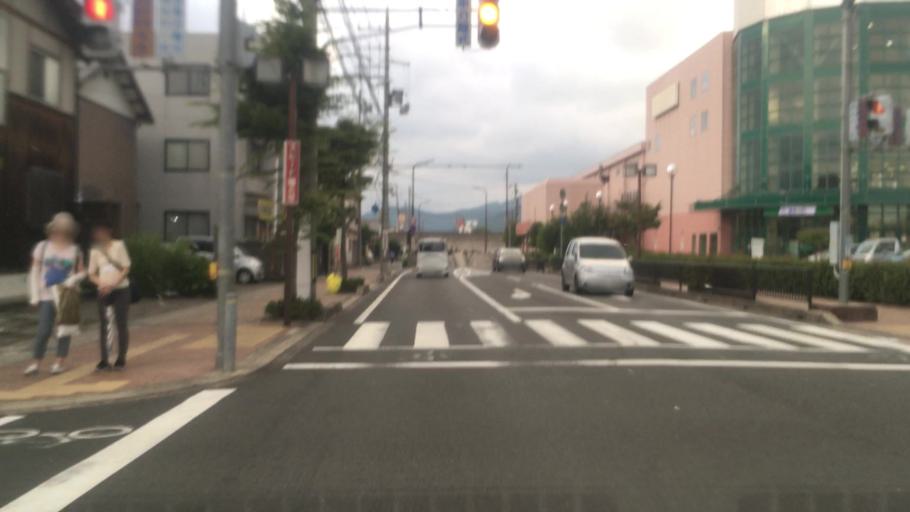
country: JP
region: Hyogo
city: Toyooka
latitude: 35.5500
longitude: 134.8155
